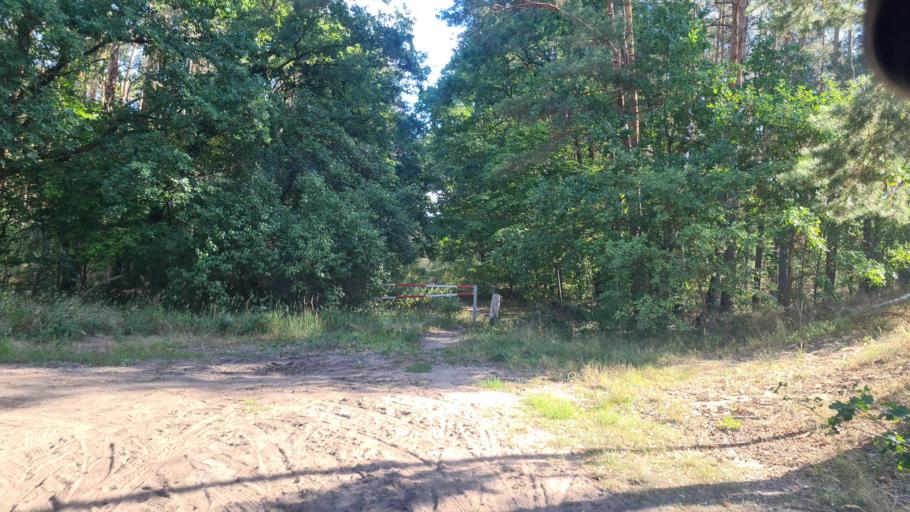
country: DE
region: Brandenburg
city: Golzow
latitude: 52.2819
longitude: 12.6109
